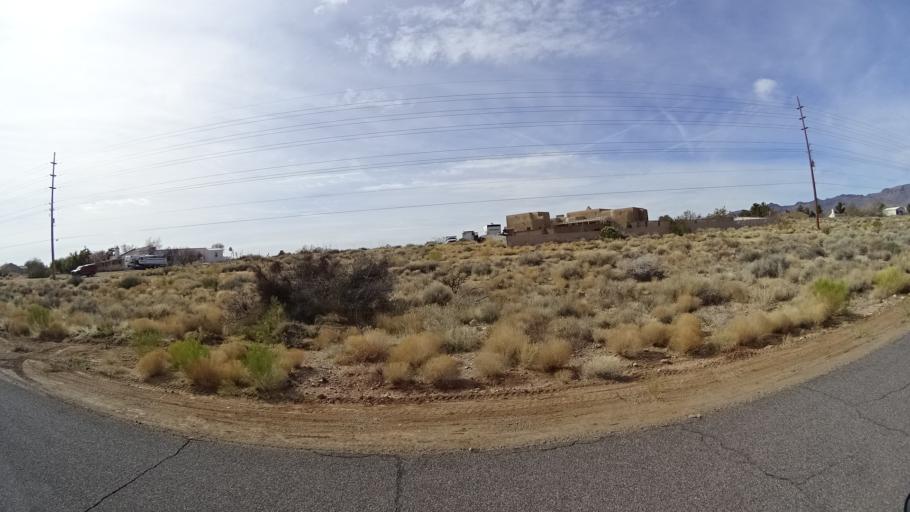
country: US
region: Arizona
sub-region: Mohave County
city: Kingman
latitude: 35.1910
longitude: -113.9852
